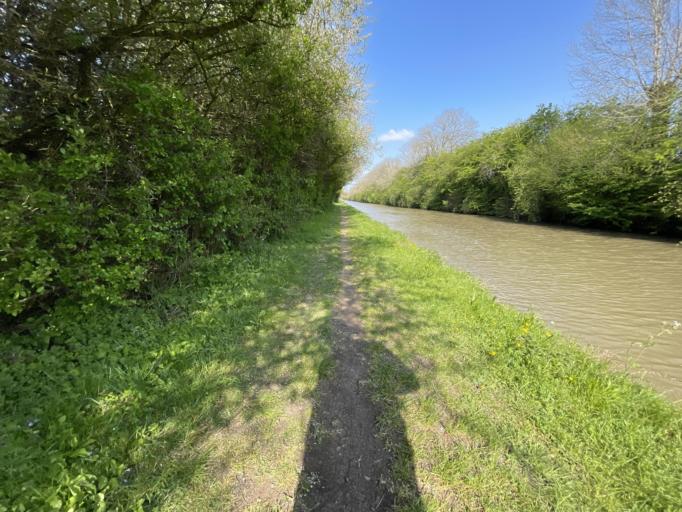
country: GB
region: England
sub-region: Warwickshire
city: Rugby
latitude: 52.3388
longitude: -1.2236
